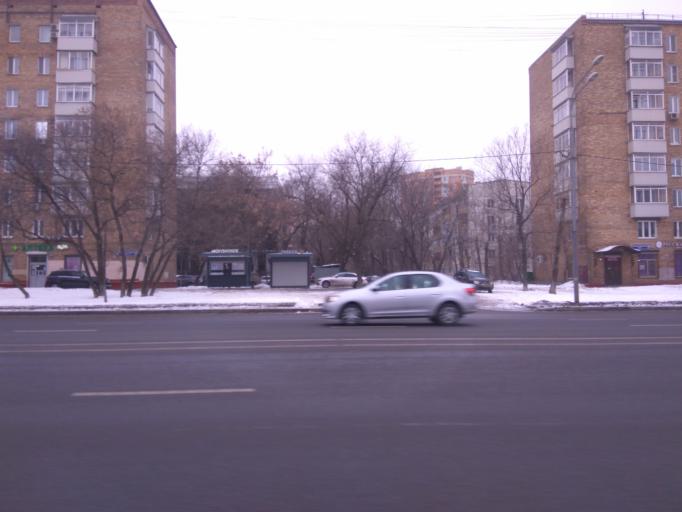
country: RU
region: Moscow
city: Taganskiy
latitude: 55.7189
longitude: 37.6636
